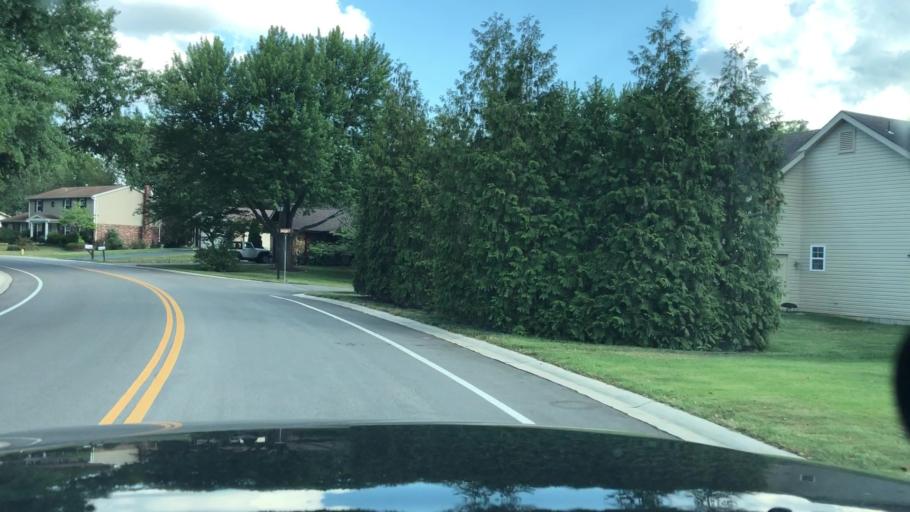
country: US
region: Missouri
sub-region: Saint Charles County
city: Lake Saint Louis
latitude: 38.7945
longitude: -90.8033
